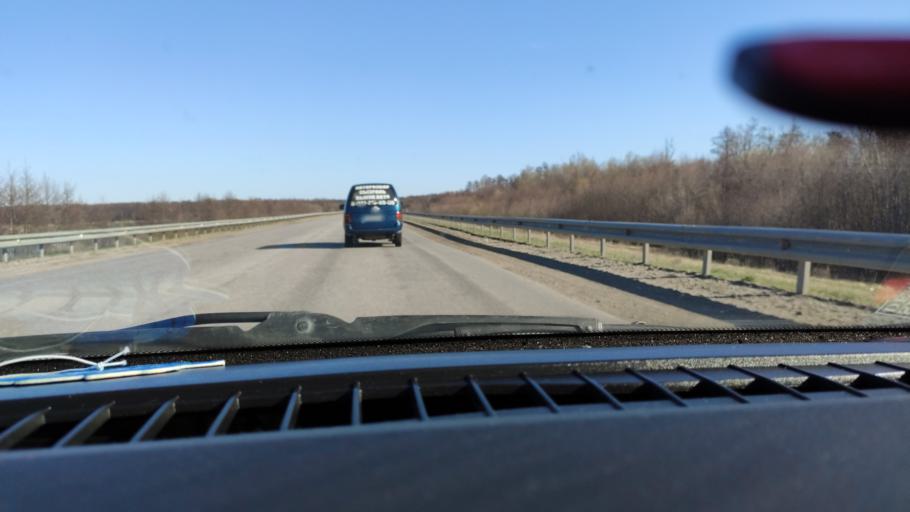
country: RU
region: Samara
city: Varlamovo
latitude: 53.1370
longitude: 48.2863
